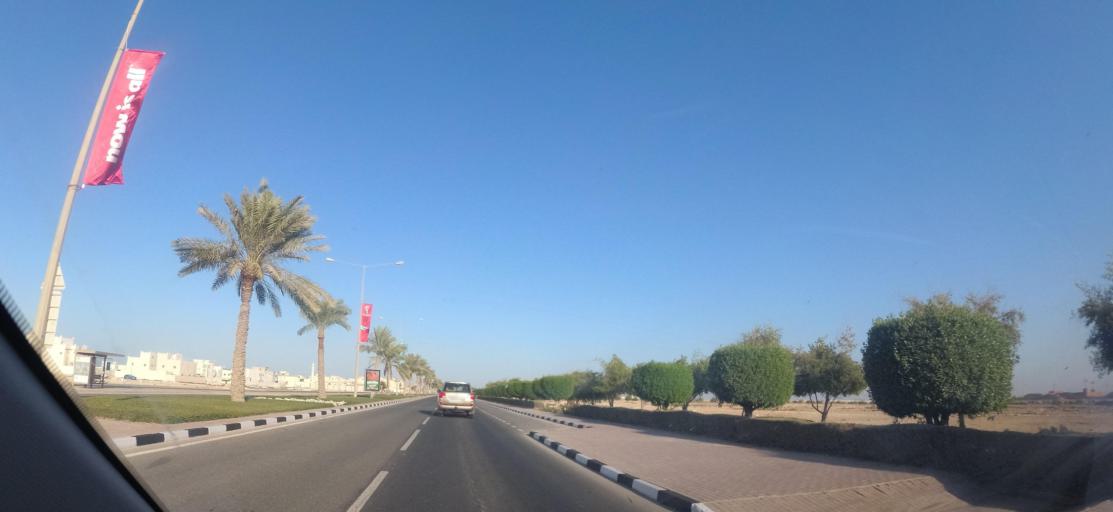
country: QA
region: Madinat ash Shamal
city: Ar Ru'ays
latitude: 26.1279
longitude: 51.2098
